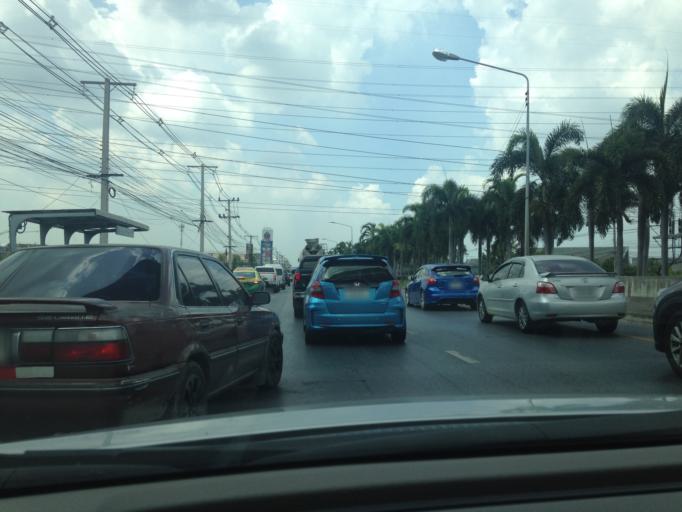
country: TH
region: Phra Nakhon Si Ayutthaya
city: Ban Bang Kadi Pathum Thani
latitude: 13.9881
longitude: 100.5849
